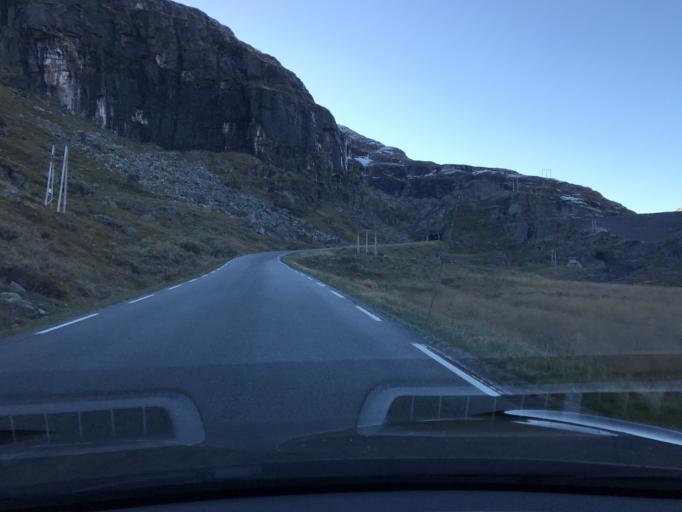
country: NO
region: Sogn og Fjordane
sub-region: Laerdal
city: Laerdalsoyri
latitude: 60.8027
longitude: 7.5656
